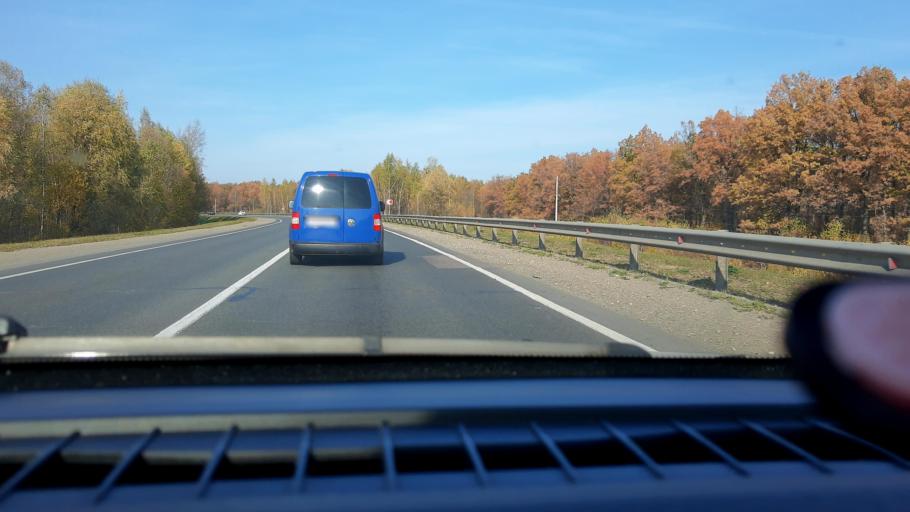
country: RU
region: Nizjnij Novgorod
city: Pamyat' Parizhskoy Kommuny
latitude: 56.0754
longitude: 44.3710
